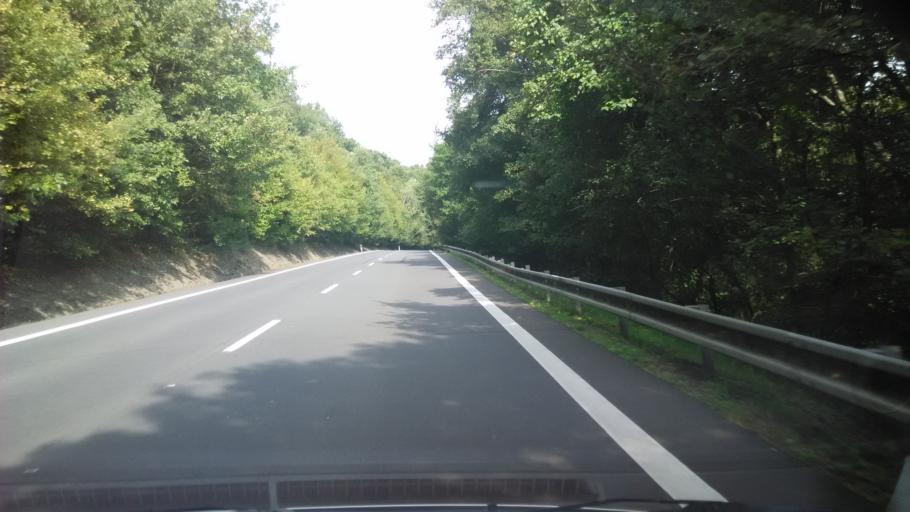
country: SK
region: Banskobystricky
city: Dudince
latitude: 48.2548
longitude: 18.9750
